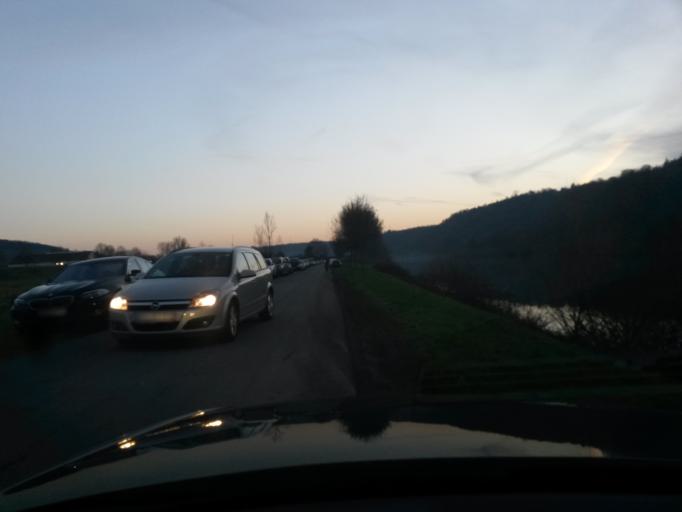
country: DE
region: Bavaria
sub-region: Regierungsbezirk Unterfranken
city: Sommerhausen
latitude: 49.7000
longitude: 10.0224
